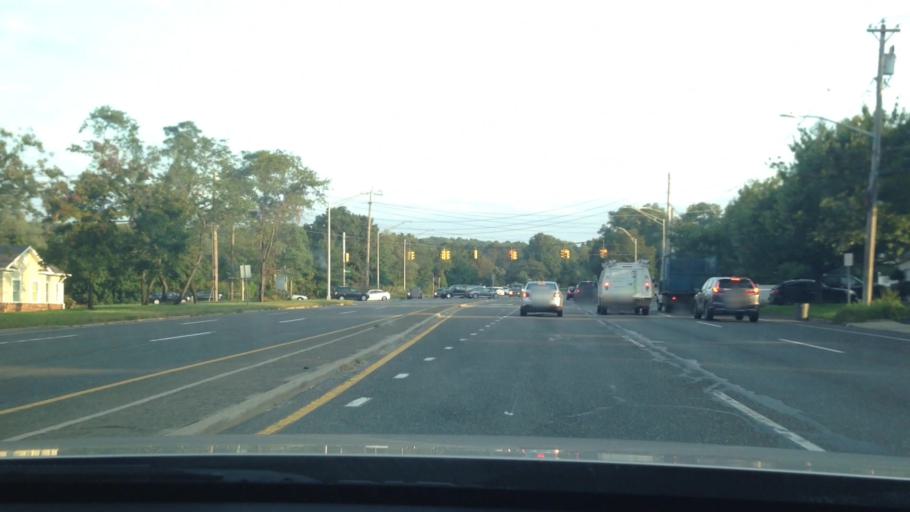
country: US
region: New York
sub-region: Suffolk County
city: Farmingville
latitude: 40.8336
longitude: -73.0213
